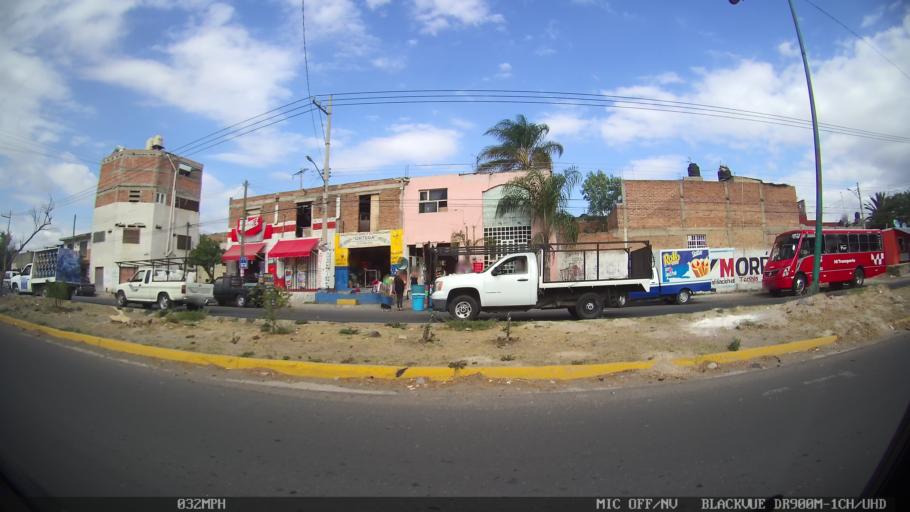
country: MX
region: Jalisco
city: Tlaquepaque
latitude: 20.6824
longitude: -103.2581
